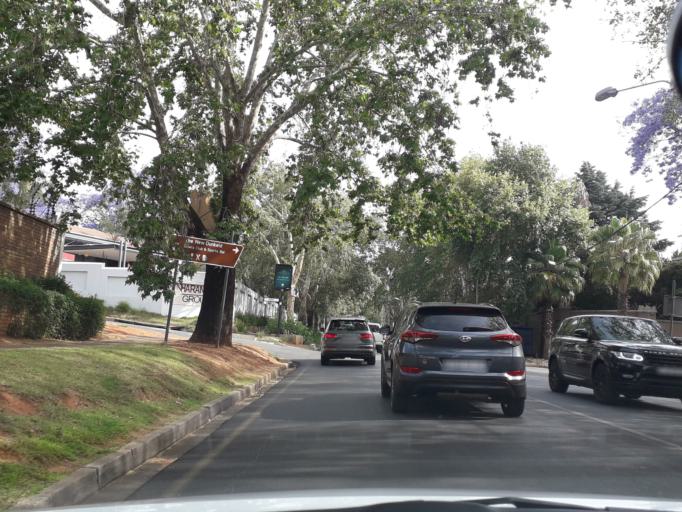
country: ZA
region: Gauteng
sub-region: City of Johannesburg Metropolitan Municipality
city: Johannesburg
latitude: -26.1341
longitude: 28.0354
